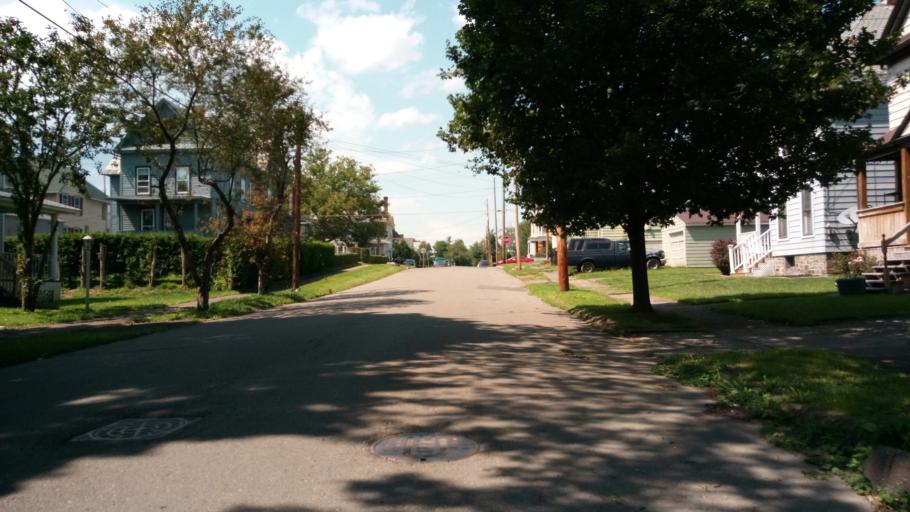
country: US
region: New York
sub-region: Chemung County
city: Elmira
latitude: 42.0838
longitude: -76.8184
